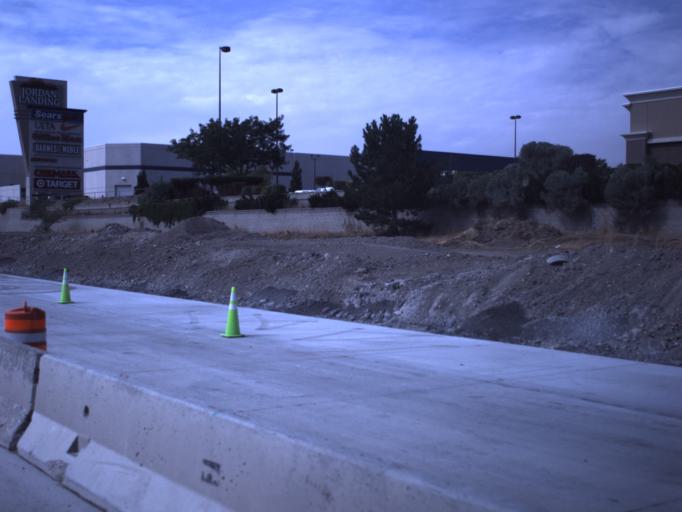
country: US
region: Utah
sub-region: Salt Lake County
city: West Jordan
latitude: 40.6179
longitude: -111.9765
